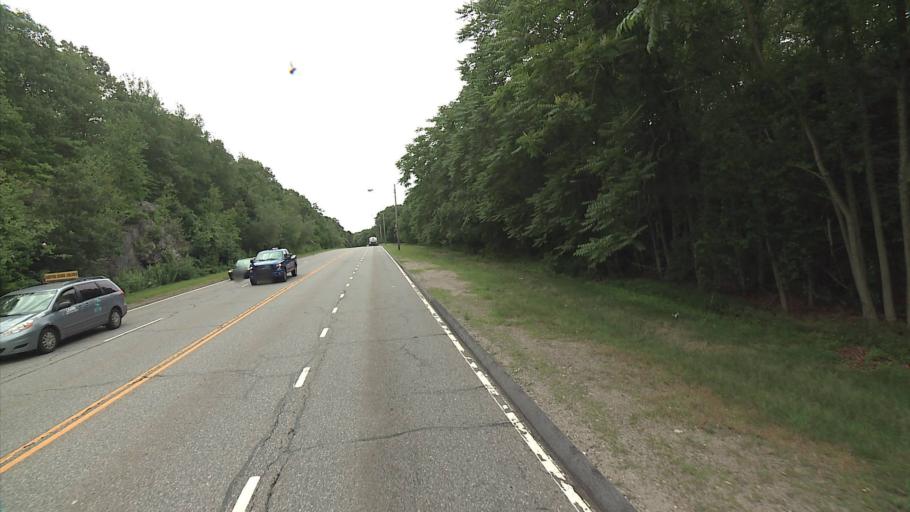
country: US
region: Connecticut
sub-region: New London County
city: Groton
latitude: 41.3492
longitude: -72.0696
